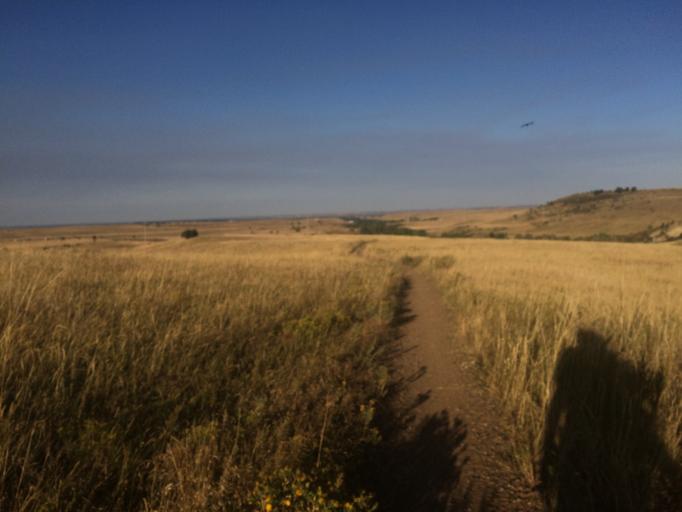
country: US
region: Colorado
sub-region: Boulder County
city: Superior
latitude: 39.9197
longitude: -105.2415
